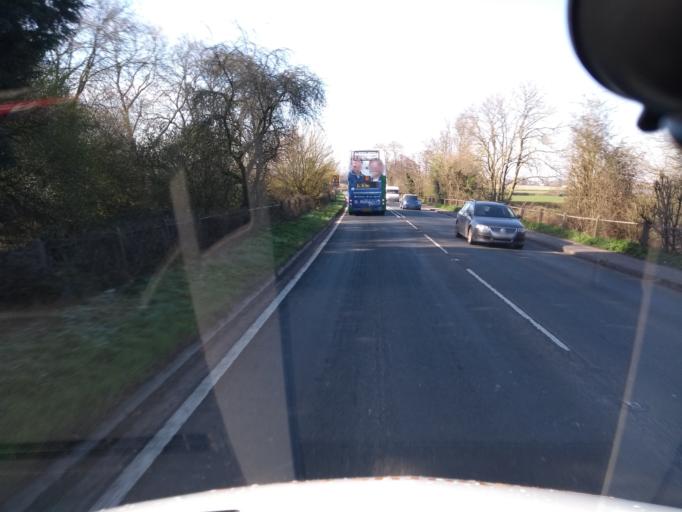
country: GB
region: England
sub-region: Somerset
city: Taunton
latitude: 50.9980
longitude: -3.1654
